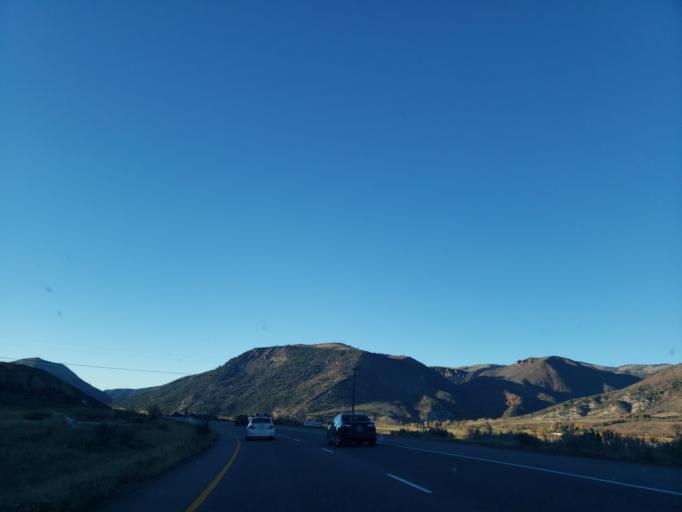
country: US
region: Colorado
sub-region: Pitkin County
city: Snowmass Village
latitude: 39.2751
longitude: -106.8928
